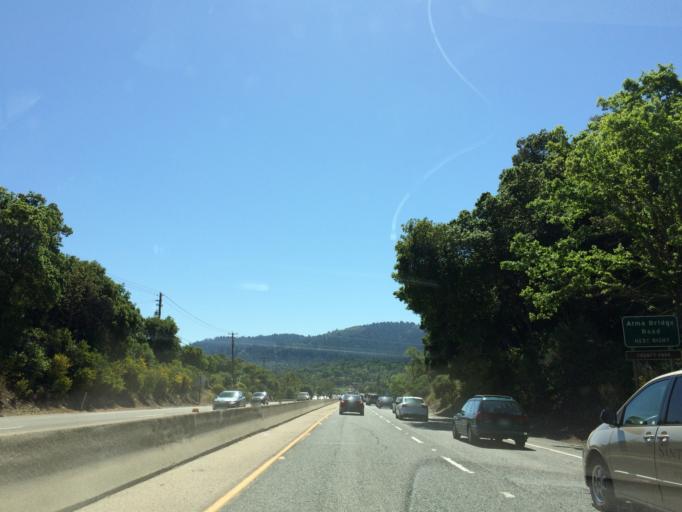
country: US
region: California
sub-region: Santa Clara County
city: Los Gatos
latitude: 37.2001
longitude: -121.9927
